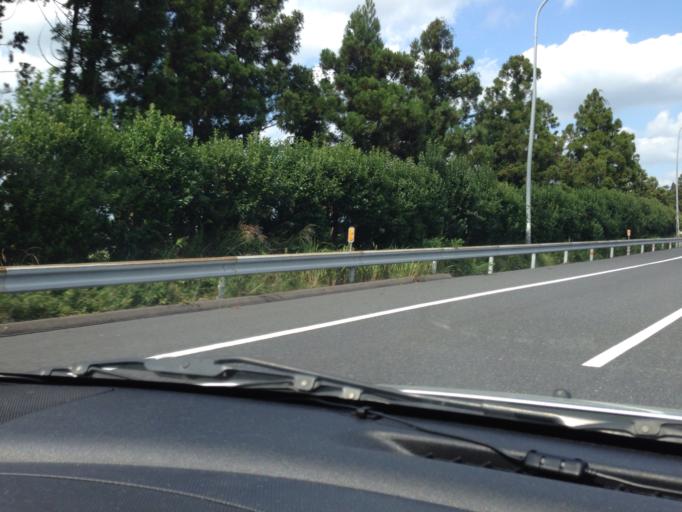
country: JP
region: Ibaraki
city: Mito-shi
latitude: 36.3787
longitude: 140.3856
